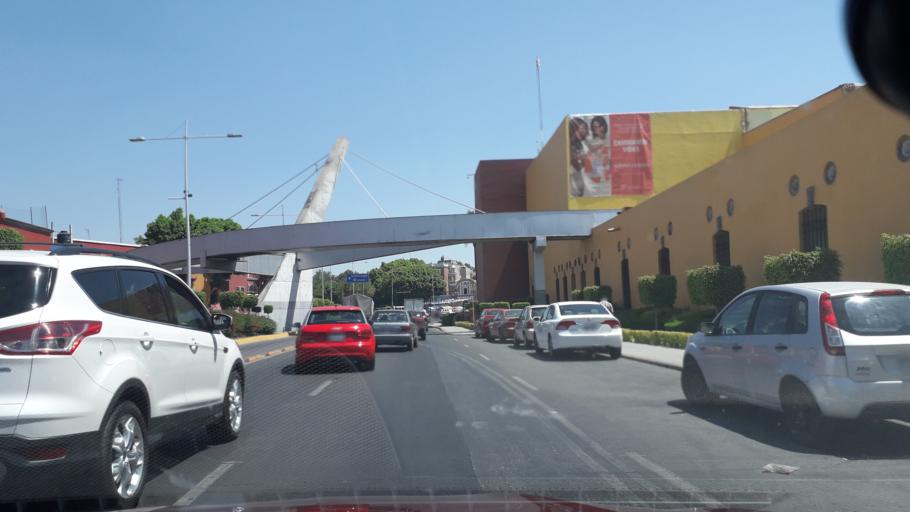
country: MX
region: Puebla
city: Puebla
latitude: 19.0434
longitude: -98.1920
